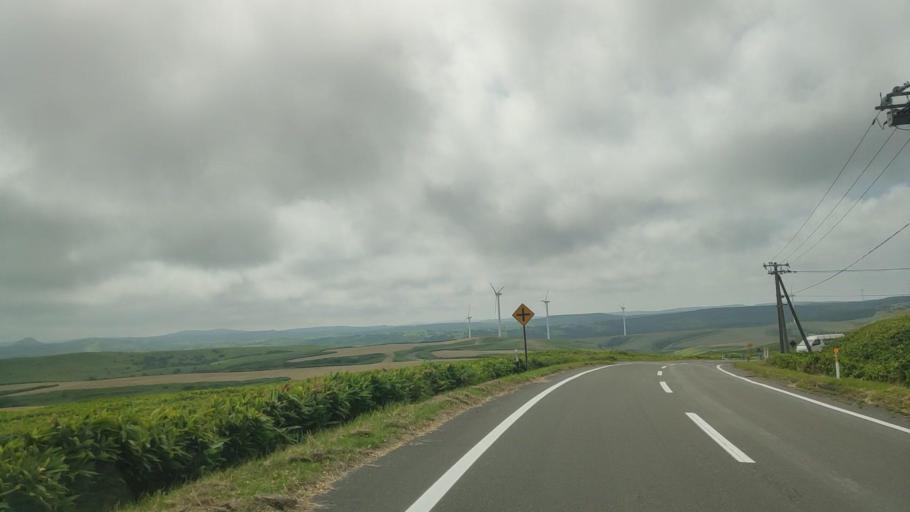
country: JP
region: Hokkaido
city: Makubetsu
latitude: 45.4872
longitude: 141.9383
